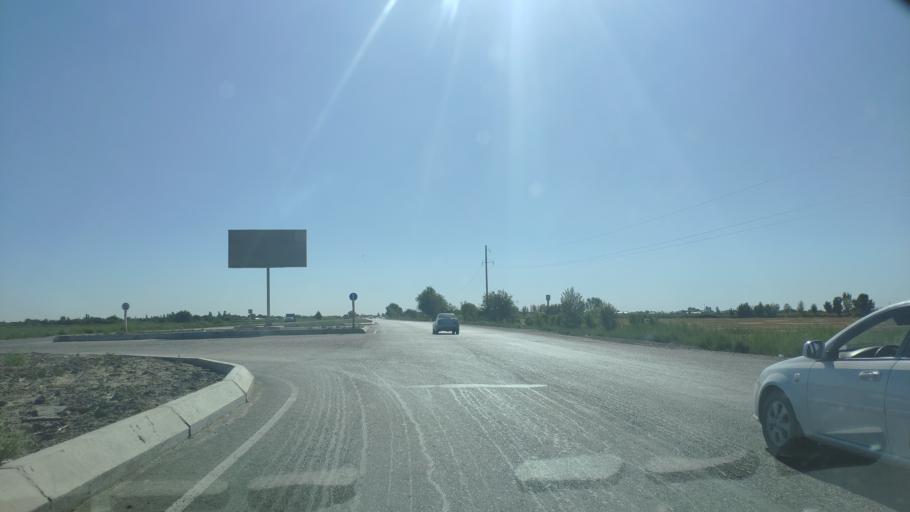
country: UZ
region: Bukhara
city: Bukhara
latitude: 39.7692
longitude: 64.3585
